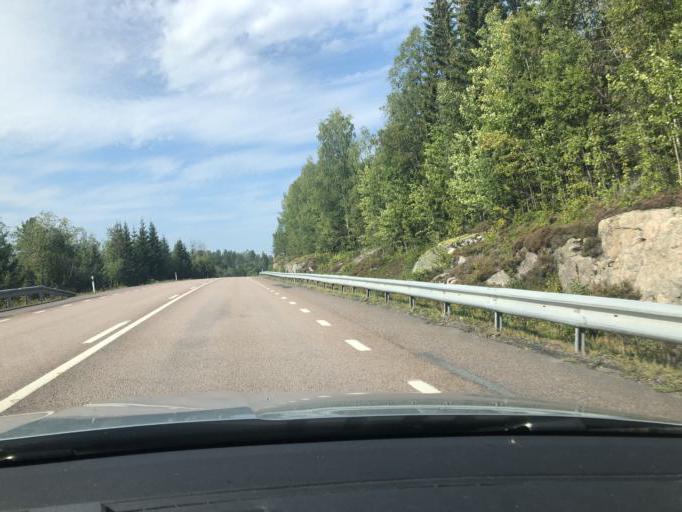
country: SE
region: Vaesternorrland
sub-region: Haernoesands Kommun
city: Haernoesand
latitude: 62.7930
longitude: 17.9040
